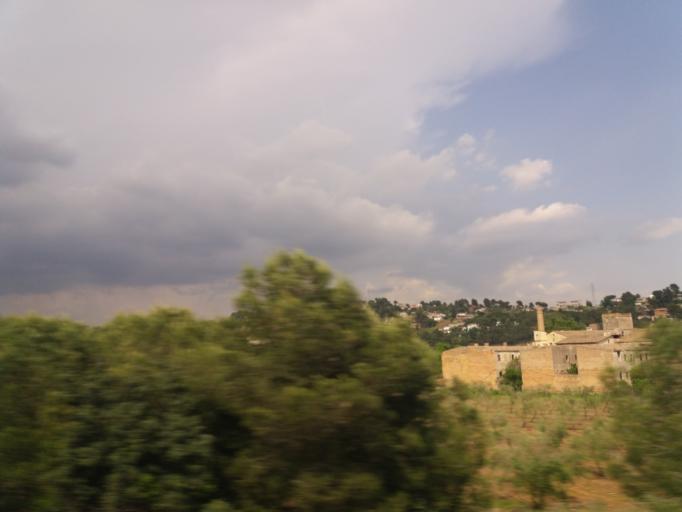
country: ES
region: Catalonia
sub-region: Provincia de Barcelona
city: Martorell
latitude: 41.4968
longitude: 1.9199
